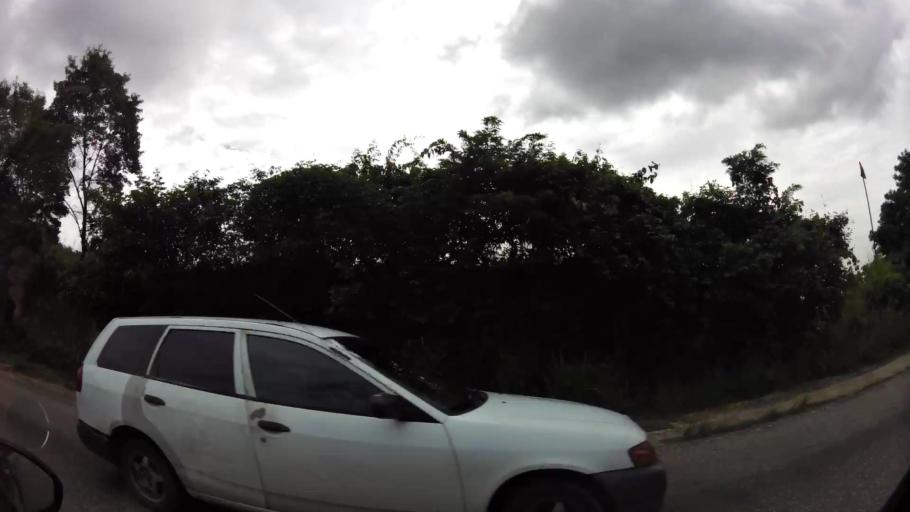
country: TT
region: City of Port of Spain
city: Port-of-Spain
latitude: 10.6750
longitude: -61.4998
